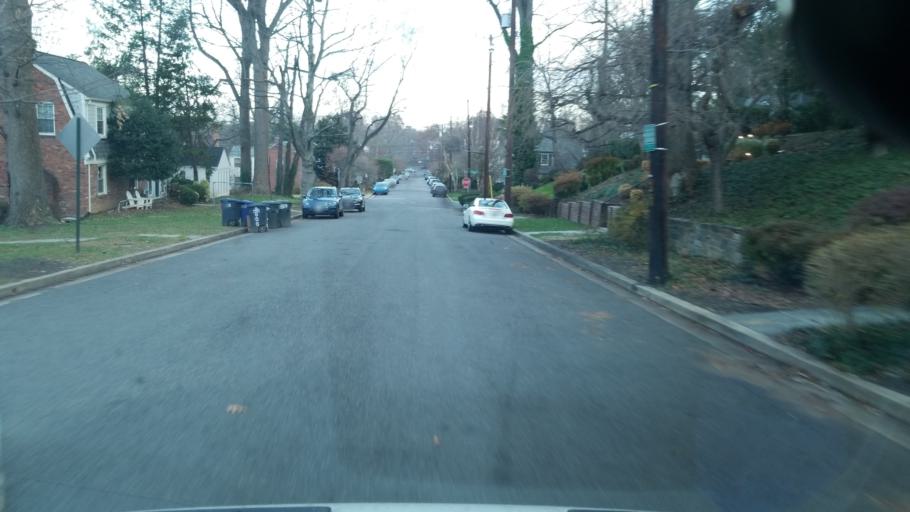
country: US
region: Maryland
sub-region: Montgomery County
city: Friendship Village
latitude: 38.9396
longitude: -77.0926
